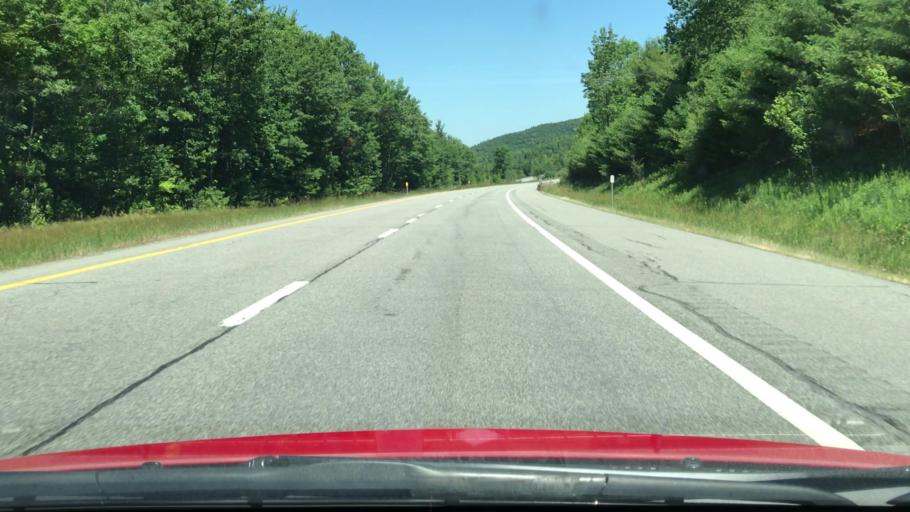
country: US
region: New York
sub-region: Essex County
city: Elizabethtown
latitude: 44.1710
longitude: -73.5833
